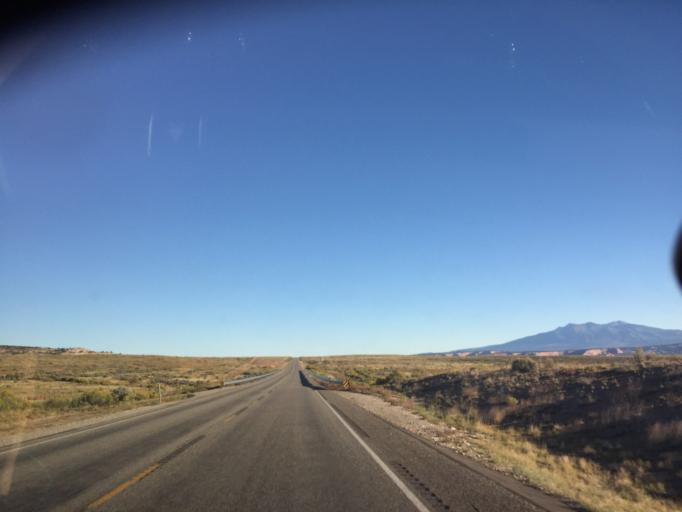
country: US
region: Utah
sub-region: San Juan County
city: Monticello
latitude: 38.1152
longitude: -109.3653
